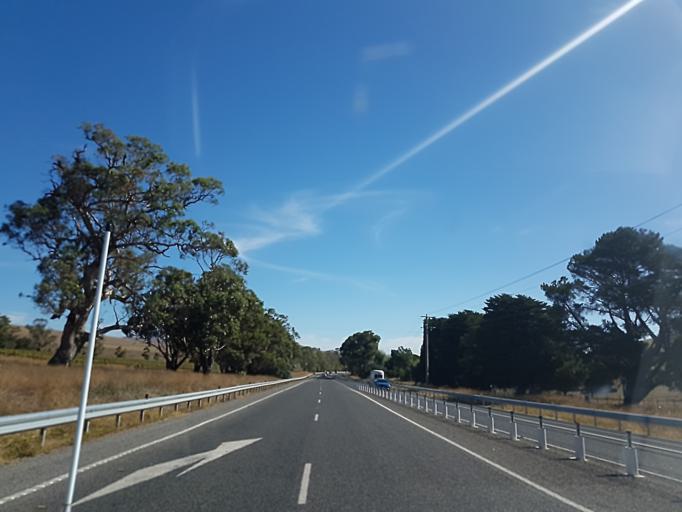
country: AU
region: Victoria
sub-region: Murrindindi
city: Alexandra
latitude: -37.2071
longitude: 145.4585
